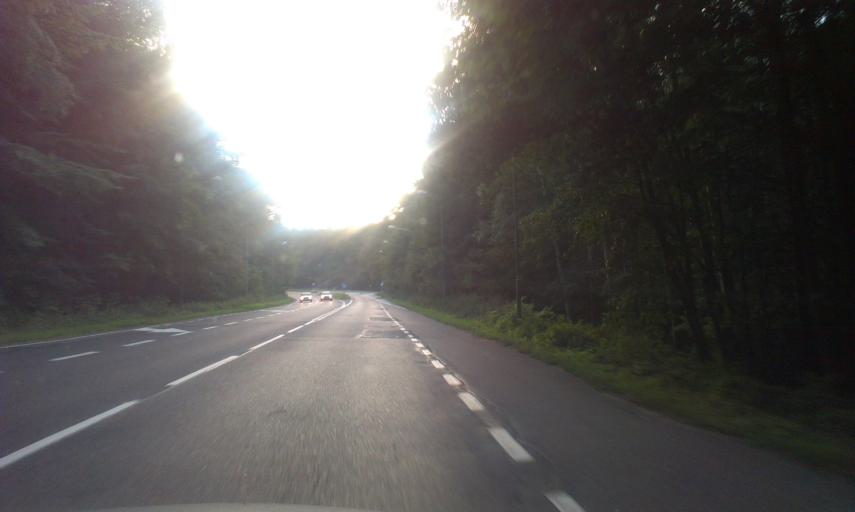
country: PL
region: West Pomeranian Voivodeship
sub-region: Powiat koszalinski
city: Sianow
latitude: 54.2233
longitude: 16.2475
